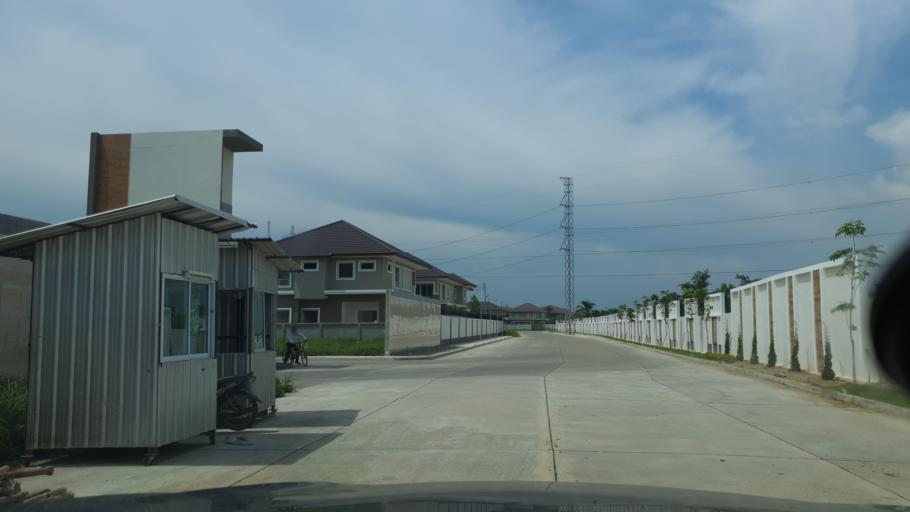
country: TH
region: Chiang Mai
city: Saraphi
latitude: 18.7385
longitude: 99.0725
